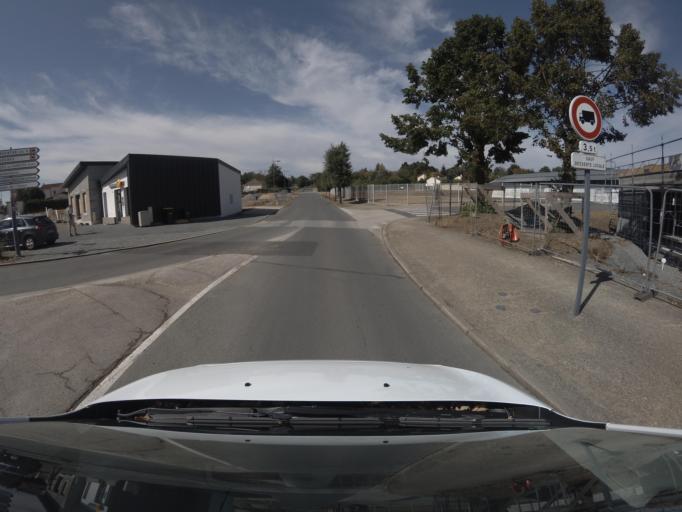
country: FR
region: Poitou-Charentes
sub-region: Departement des Deux-Sevres
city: Nueil-les-Aubiers
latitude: 46.9463
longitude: -0.5941
